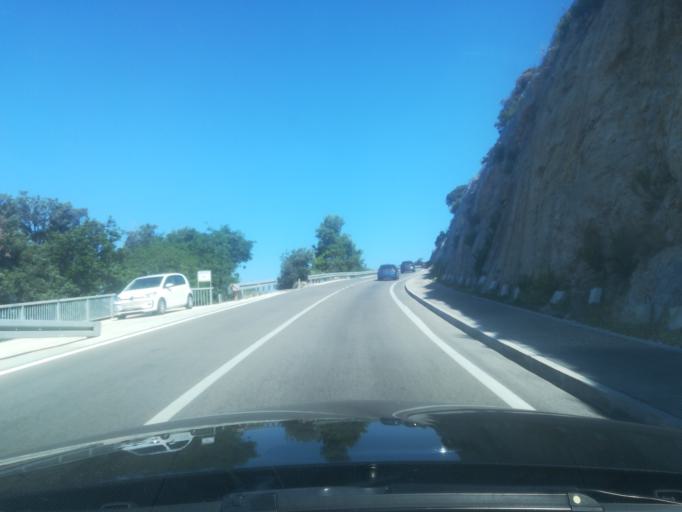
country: HR
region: Primorsko-Goranska
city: Supetarska Draga
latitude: 44.8108
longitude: 14.7180
